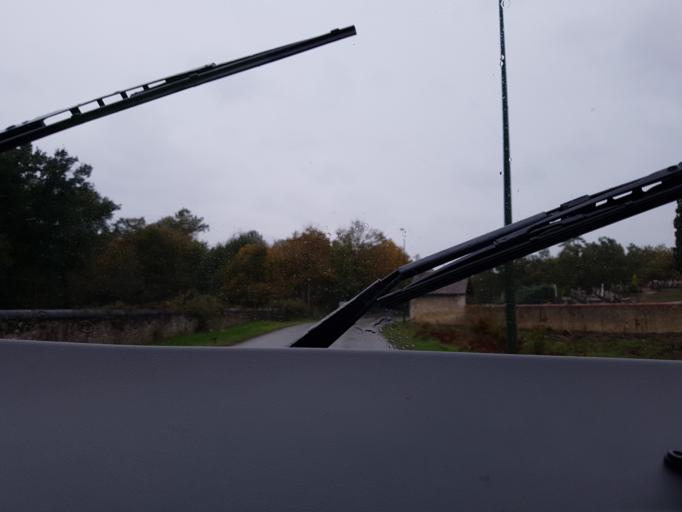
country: FR
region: Aquitaine
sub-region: Departement de la Gironde
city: Saint-Symphorien
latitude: 44.3258
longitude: -0.5841
